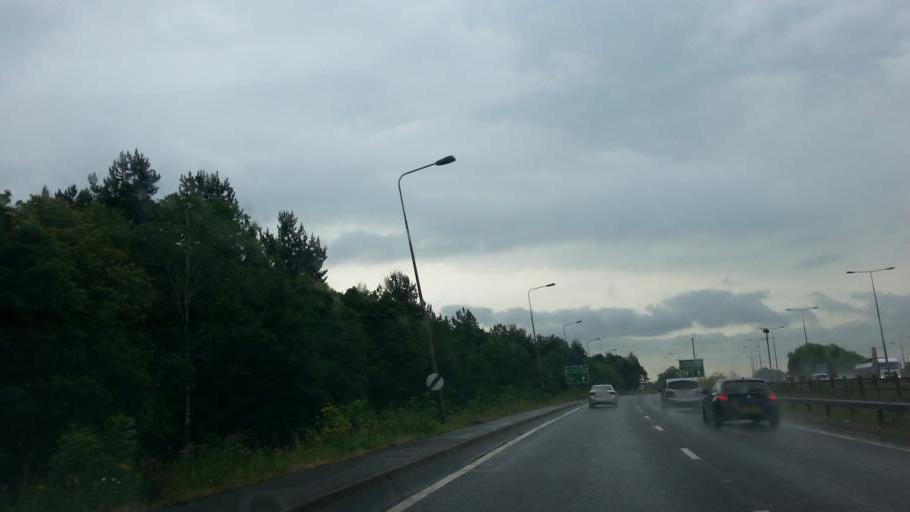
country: GB
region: England
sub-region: Cambridgeshire
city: Girton
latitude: 52.2396
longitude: 0.0602
